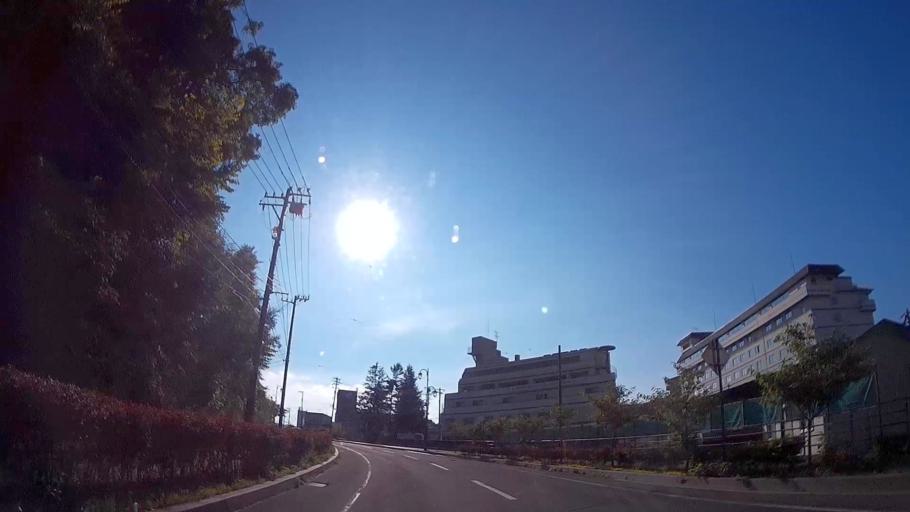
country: JP
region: Hokkaido
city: Date
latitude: 42.5650
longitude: 140.8270
